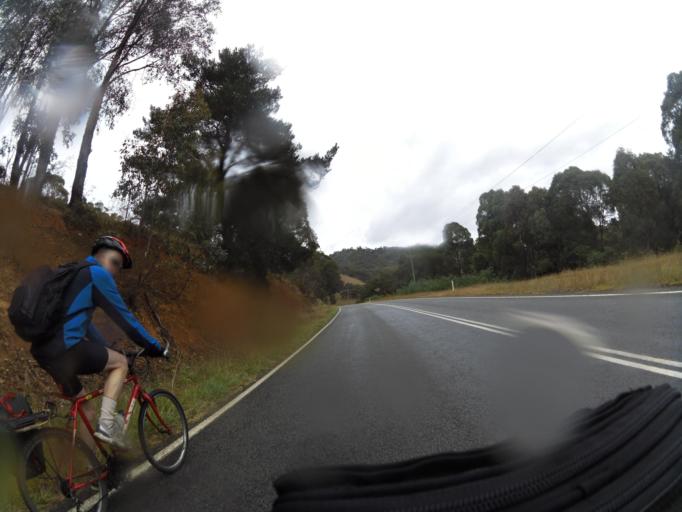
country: AU
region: New South Wales
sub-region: Greater Hume Shire
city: Holbrook
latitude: -36.2190
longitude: 147.6734
